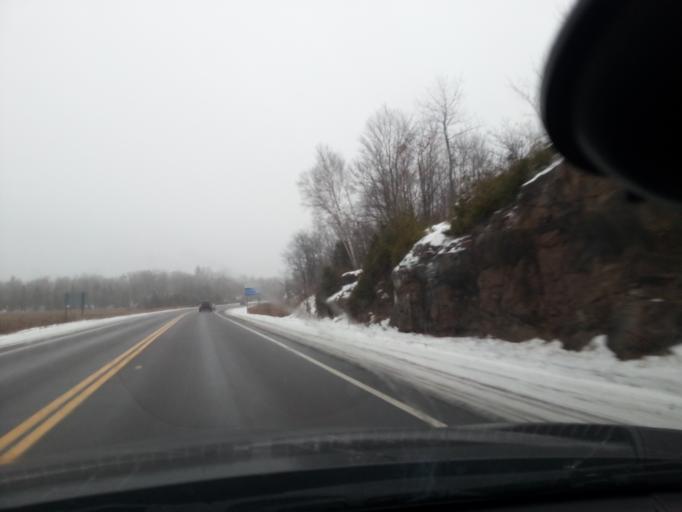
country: CA
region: Ontario
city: Perth
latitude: 44.7918
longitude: -76.7029
